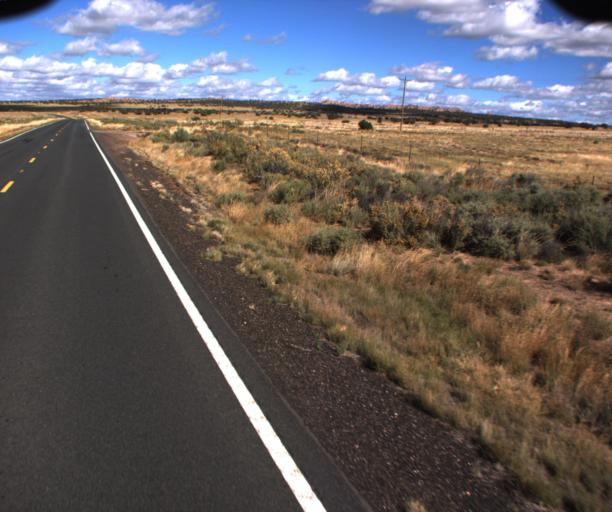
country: US
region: Arizona
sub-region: Apache County
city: Houck
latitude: 35.0542
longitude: -109.2760
